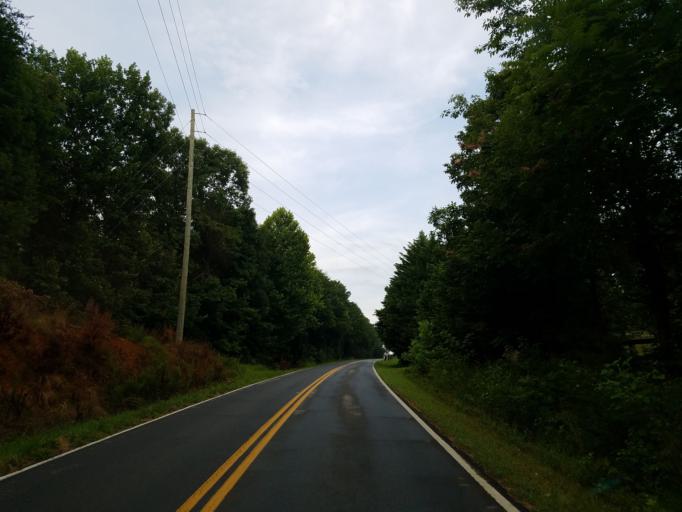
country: US
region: Georgia
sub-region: Pickens County
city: Jasper
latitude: 34.4530
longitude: -84.5501
